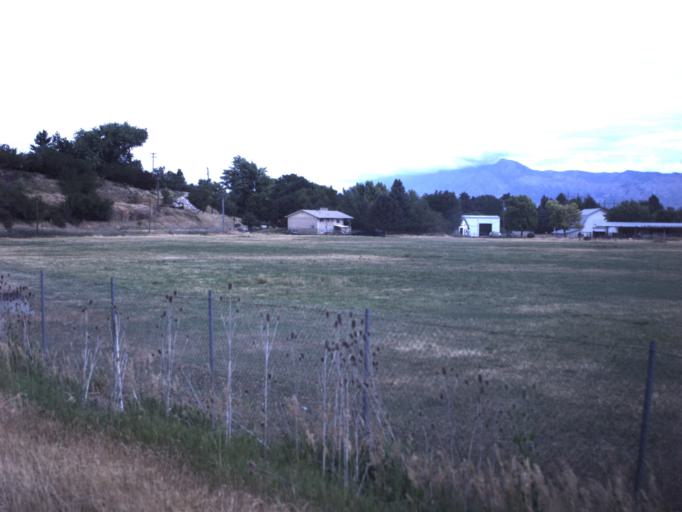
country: US
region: Utah
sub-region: Weber County
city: Riverdale
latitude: 41.1602
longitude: -112.0044
